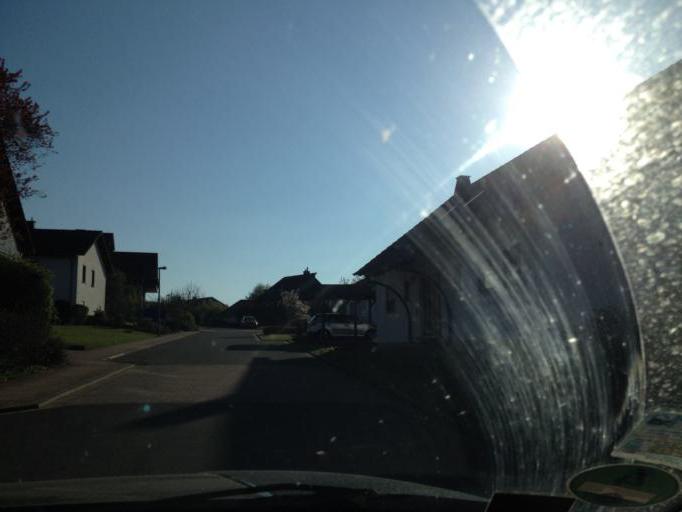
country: DE
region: Saarland
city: Sankt Wendel
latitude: 49.4805
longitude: 7.1829
